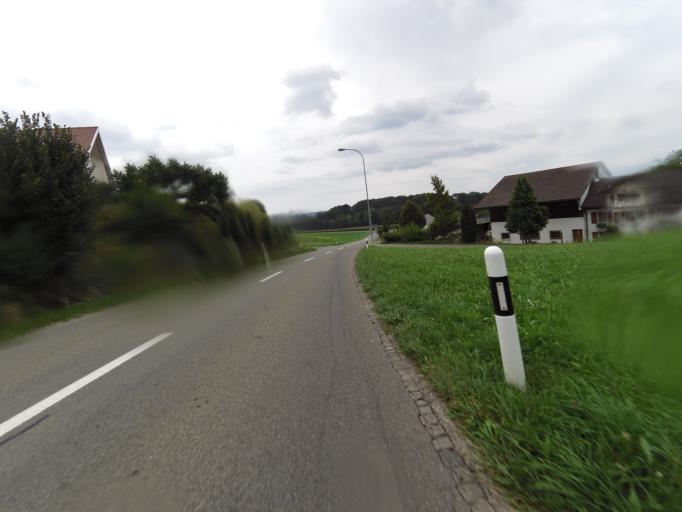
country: CH
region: Thurgau
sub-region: Weinfelden District
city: Wigoltingen
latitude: 47.6174
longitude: 9.0400
